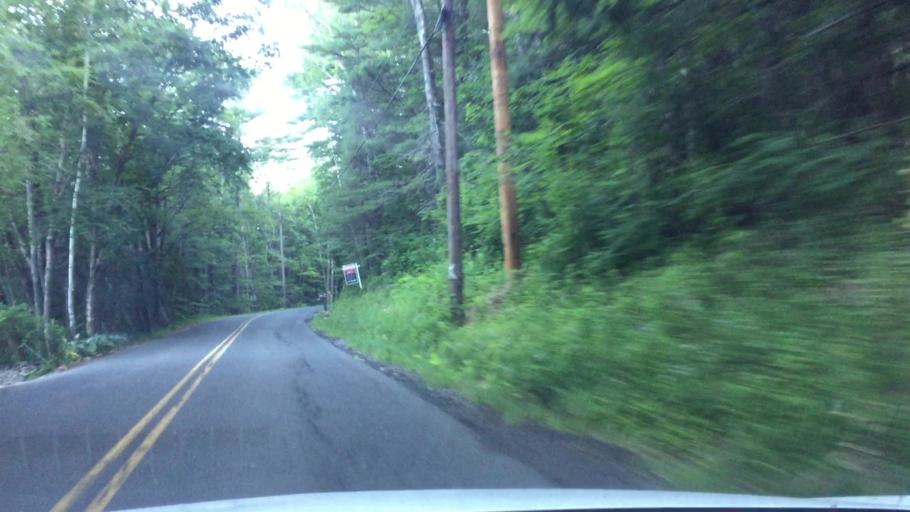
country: US
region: Massachusetts
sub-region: Berkshire County
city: Otis
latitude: 42.2389
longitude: -73.1133
